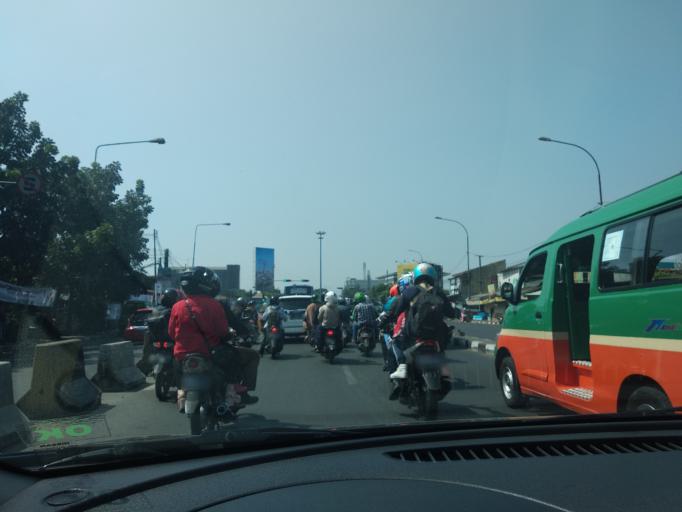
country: ID
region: West Java
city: Margahayukencana
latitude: -6.9470
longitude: 107.5943
